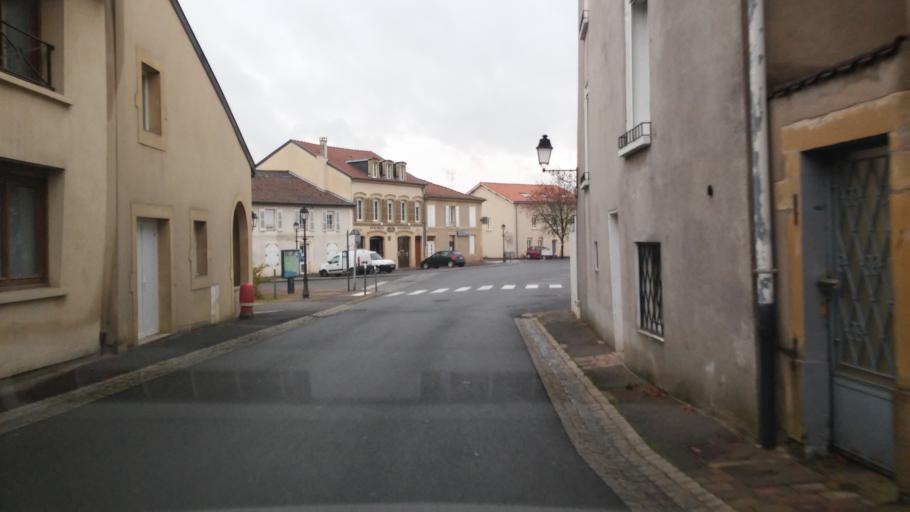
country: FR
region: Lorraine
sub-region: Departement de la Moselle
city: Vigy
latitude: 49.2027
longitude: 6.2968
